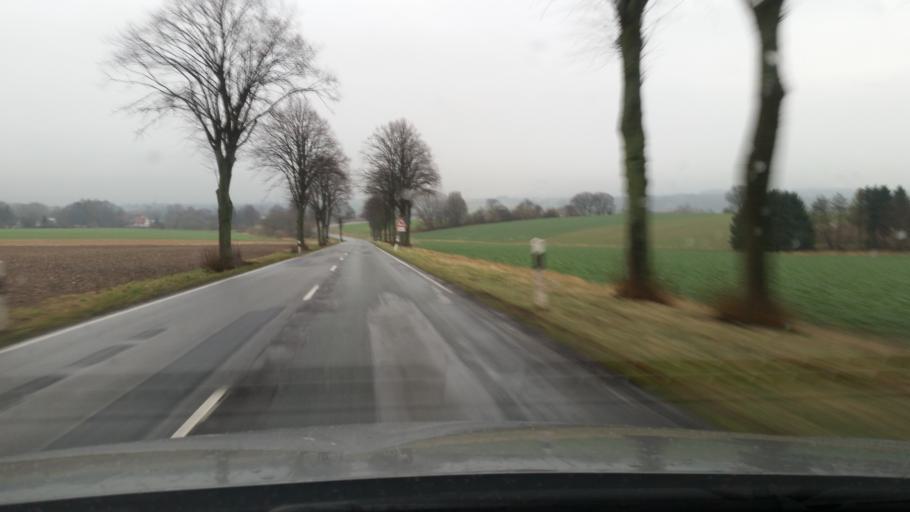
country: DE
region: Lower Saxony
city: Bad Munder am Deister
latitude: 52.1451
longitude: 9.4343
